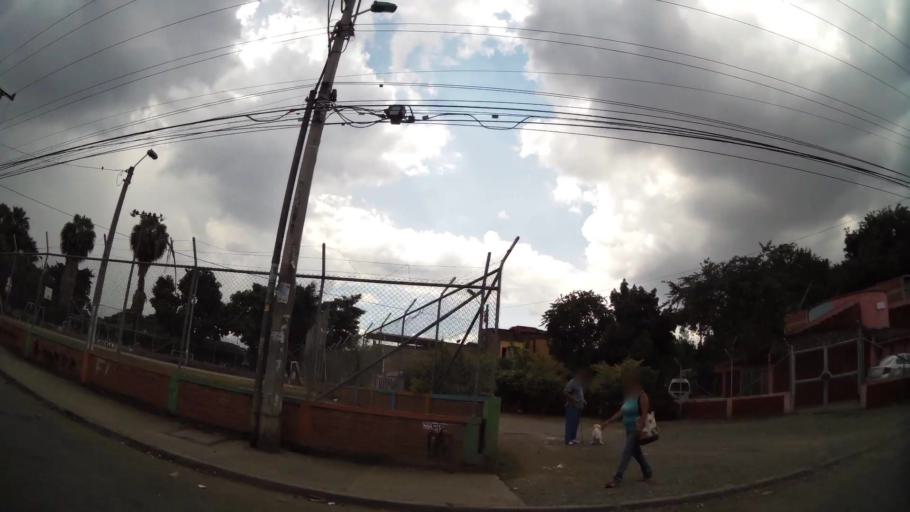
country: CO
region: Valle del Cauca
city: Cali
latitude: 3.4543
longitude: -76.4869
